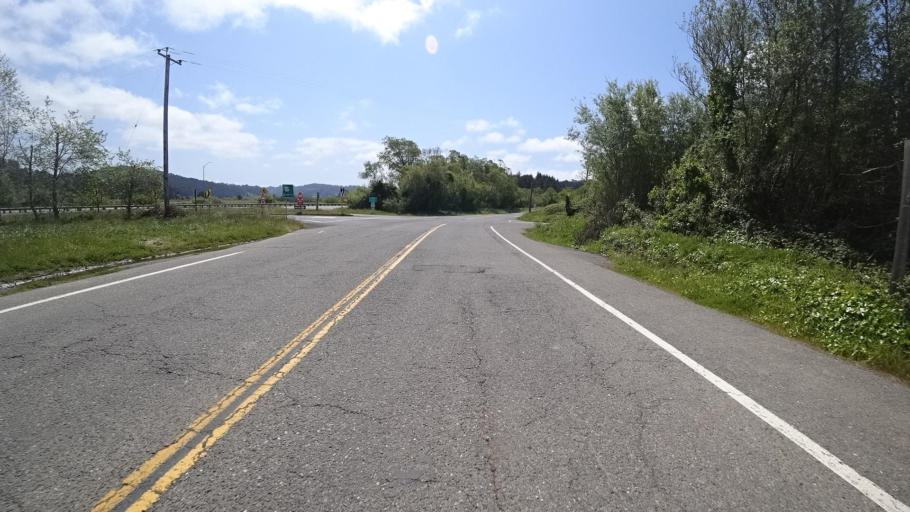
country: US
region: California
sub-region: Humboldt County
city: Humboldt Hill
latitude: 40.6705
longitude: -124.2028
